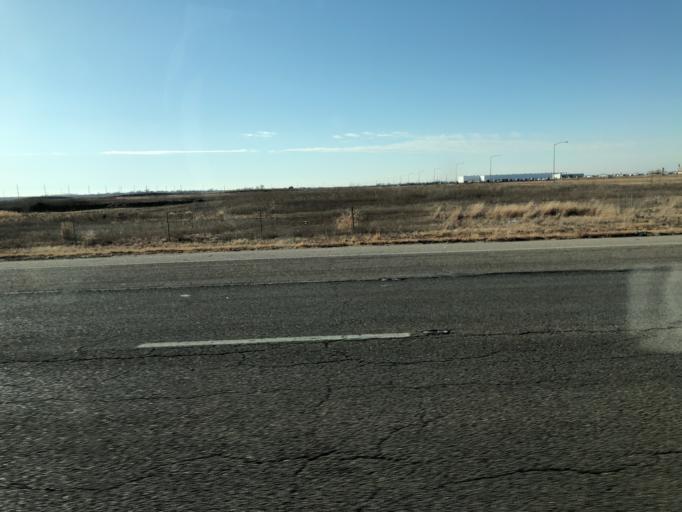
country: US
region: Kansas
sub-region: Reno County
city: Hutchinson
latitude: 38.0329
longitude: -97.8669
